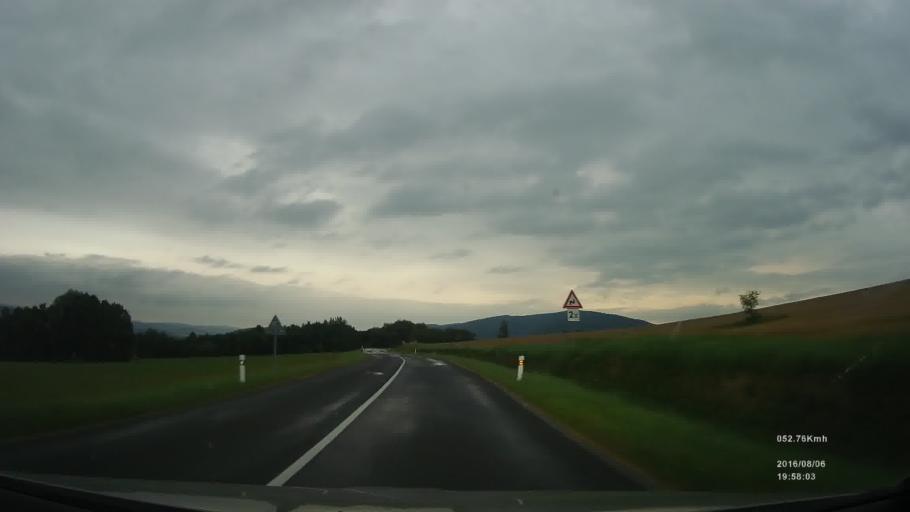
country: SK
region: Presovsky
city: Svidnik
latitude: 49.2718
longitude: 21.5792
